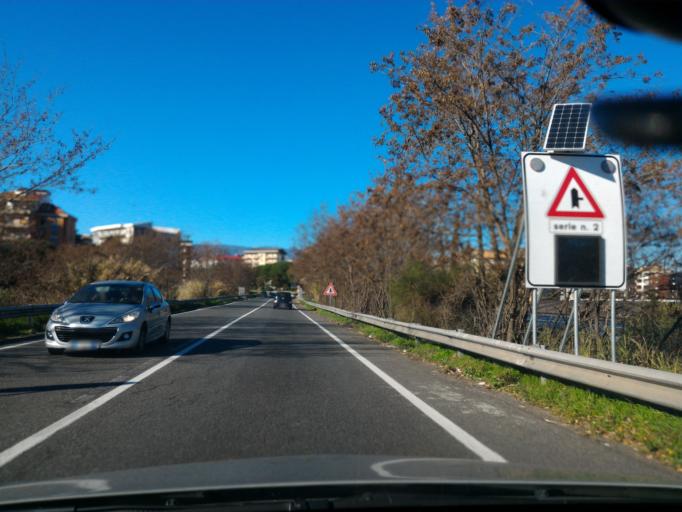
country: IT
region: Calabria
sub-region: Provincia di Cosenza
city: Quattromiglia
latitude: 39.3292
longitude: 16.2491
